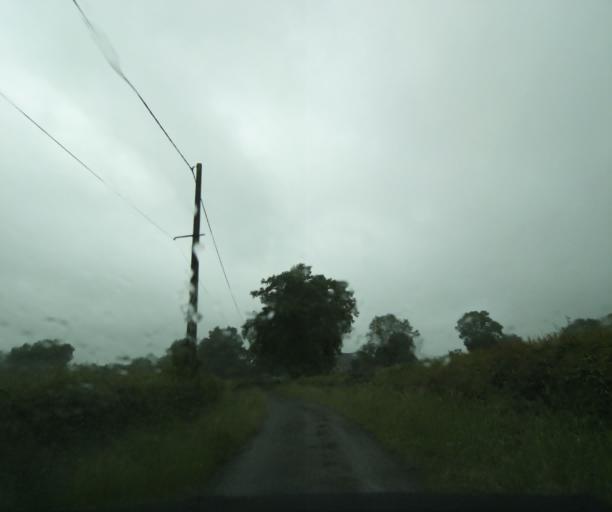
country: FR
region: Bourgogne
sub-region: Departement de Saone-et-Loire
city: Ciry-le-Noble
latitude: 46.5329
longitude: 4.3636
